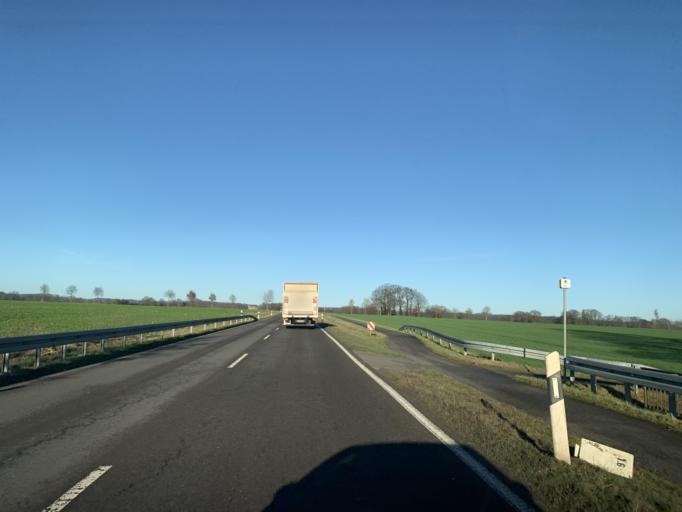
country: DE
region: North Rhine-Westphalia
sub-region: Regierungsbezirk Munster
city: Dulmen
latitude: 51.8754
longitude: 7.2885
